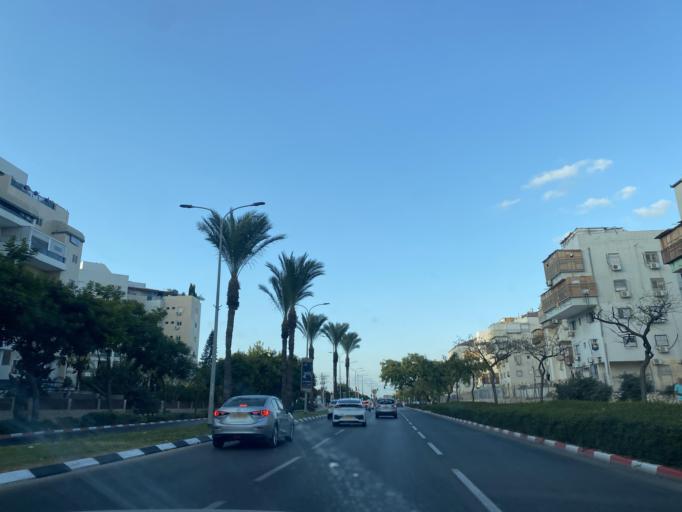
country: IL
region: Southern District
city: Ashdod
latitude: 31.7898
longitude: 34.6487
